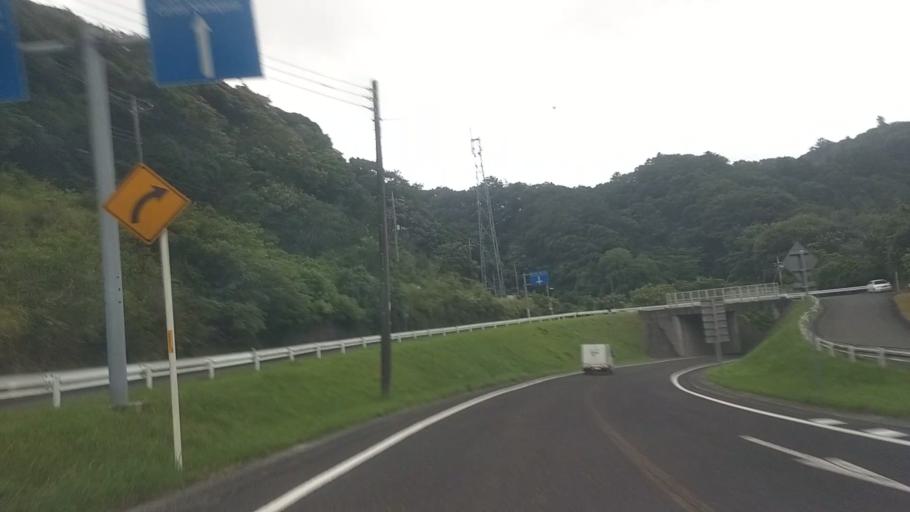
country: JP
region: Chiba
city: Kawaguchi
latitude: 35.1579
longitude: 140.0674
